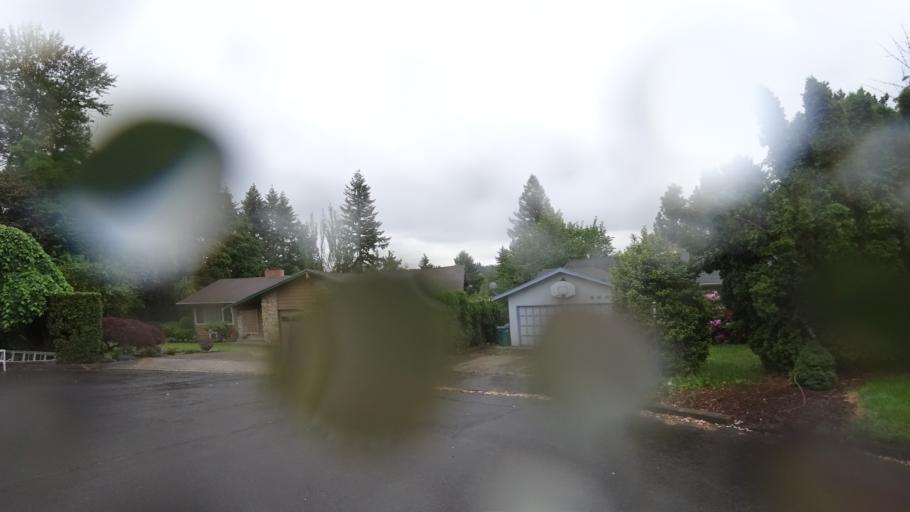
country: US
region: Oregon
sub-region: Washington County
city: Raleigh Hills
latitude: 45.4732
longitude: -122.7696
